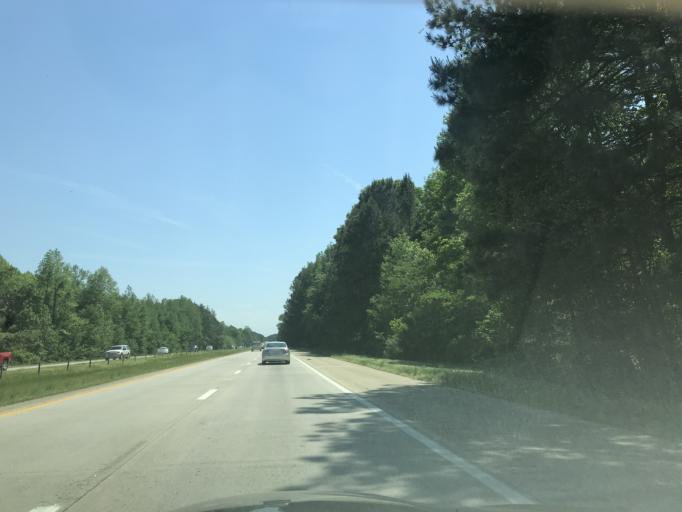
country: US
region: North Carolina
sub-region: Johnston County
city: Benson
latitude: 35.4899
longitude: -78.5525
